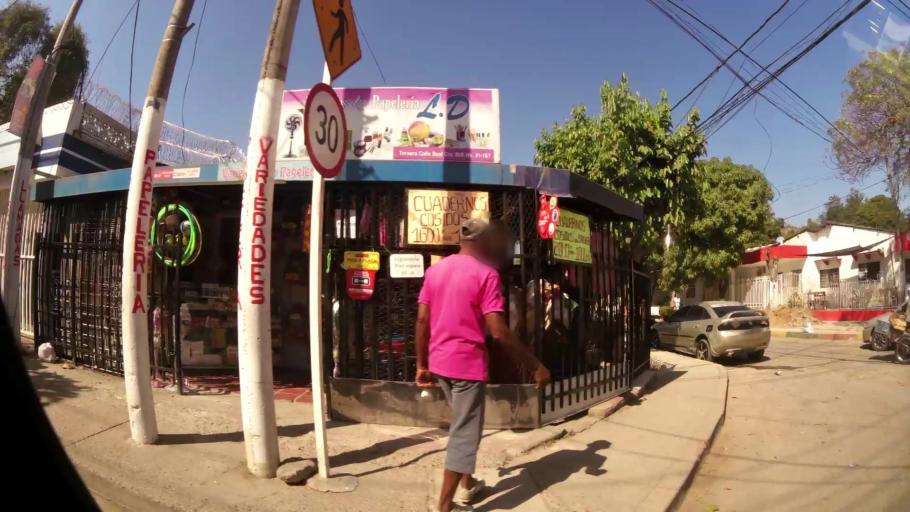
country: CO
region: Bolivar
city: Cartagena
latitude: 10.3838
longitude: -75.4658
